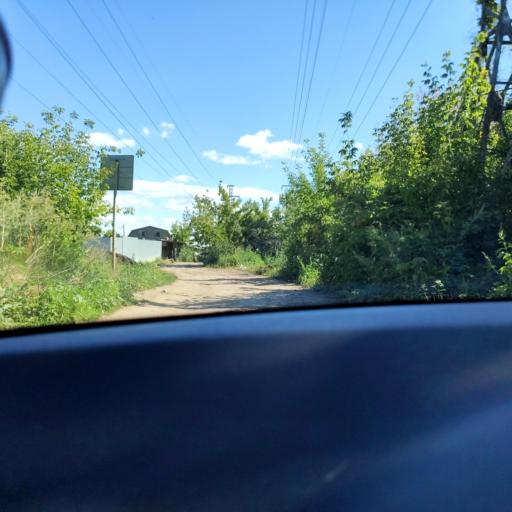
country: RU
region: Samara
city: Petra-Dubrava
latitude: 53.2942
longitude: 50.3051
